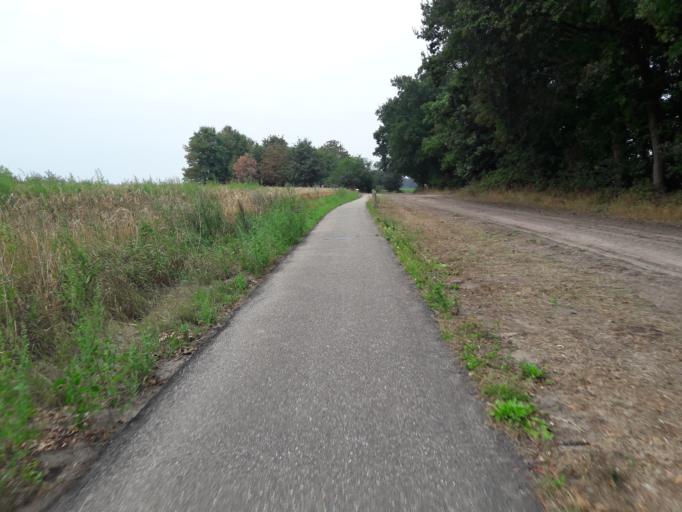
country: NL
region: Drenthe
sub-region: Gemeente Borger-Odoorn
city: Borger
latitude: 52.9405
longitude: 6.8221
